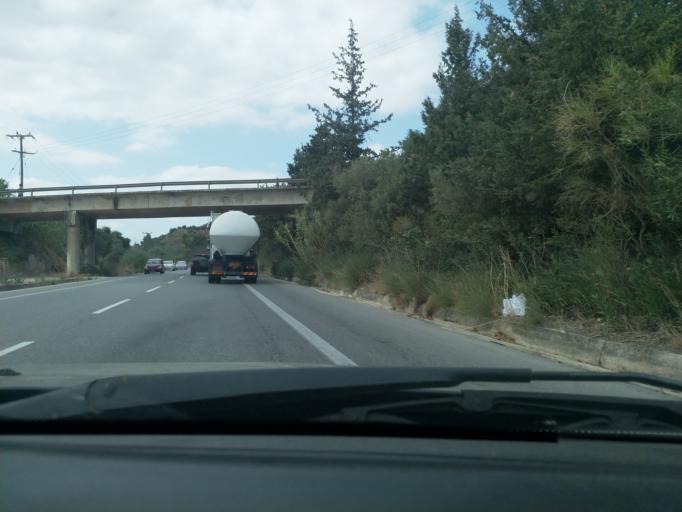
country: GR
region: Crete
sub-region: Nomos Chanias
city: Georgioupolis
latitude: 35.3760
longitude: 24.2082
